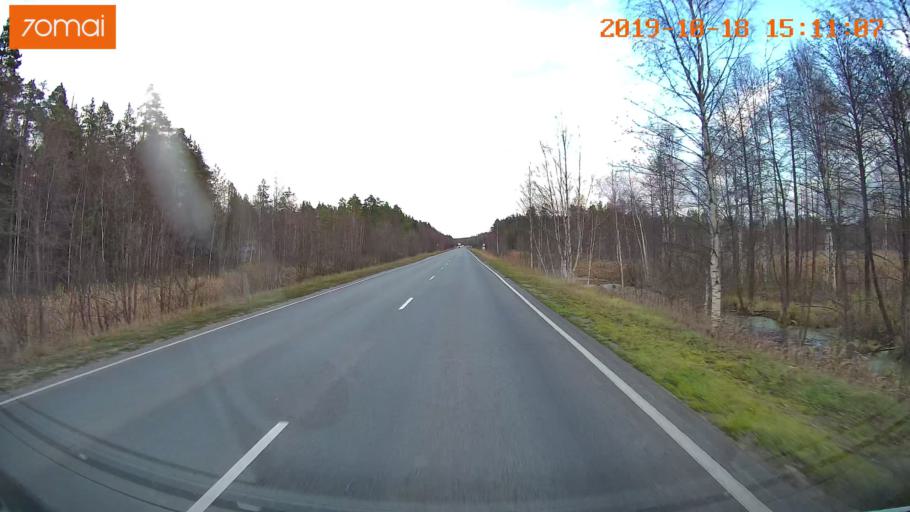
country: RU
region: Vladimir
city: Gus'-Khrustal'nyy
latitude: 55.5703
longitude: 40.6620
